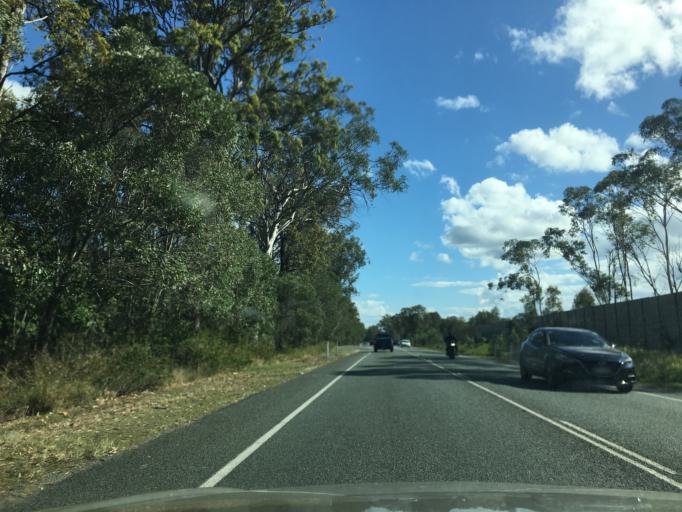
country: AU
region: Queensland
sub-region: Logan
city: Chambers Flat
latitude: -27.7757
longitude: 153.1031
